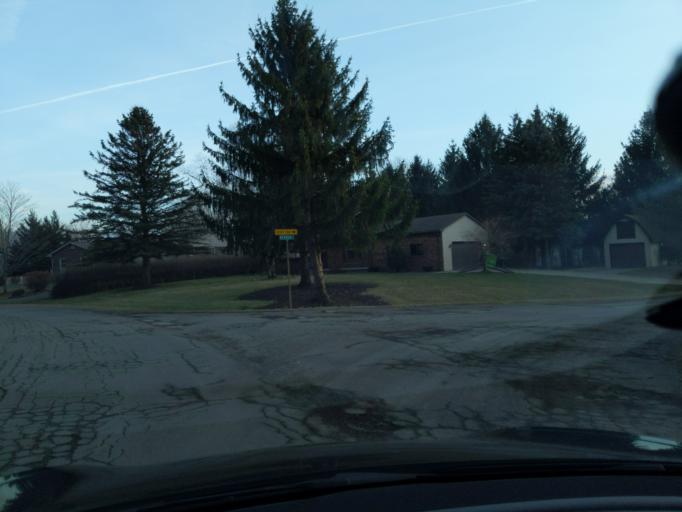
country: US
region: Michigan
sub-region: Livingston County
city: Brighton
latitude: 42.6432
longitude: -83.7215
